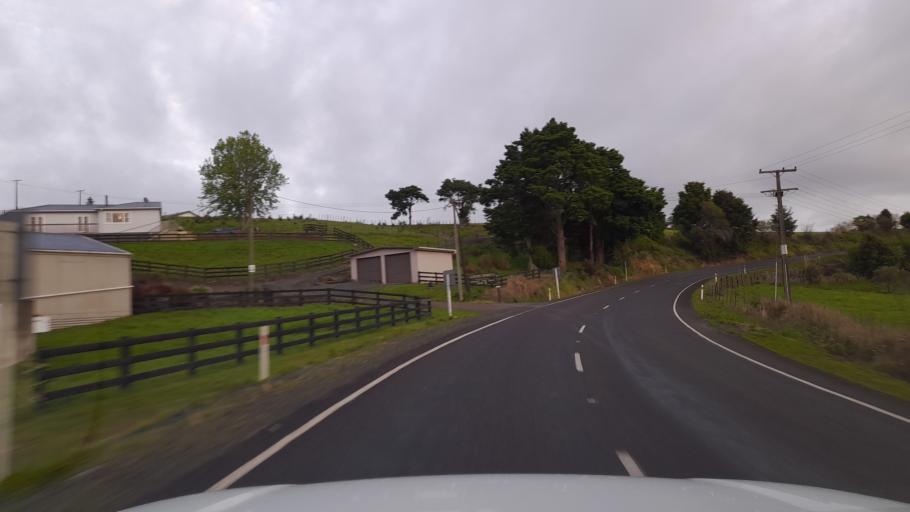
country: NZ
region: Northland
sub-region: Whangarei
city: Maungatapere
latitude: -35.7314
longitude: 174.0466
